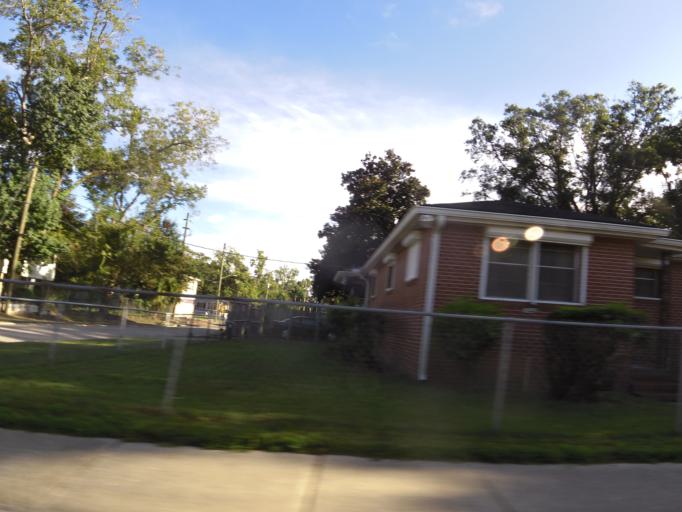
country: US
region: Florida
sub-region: Duval County
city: Jacksonville
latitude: 30.3513
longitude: -81.6930
